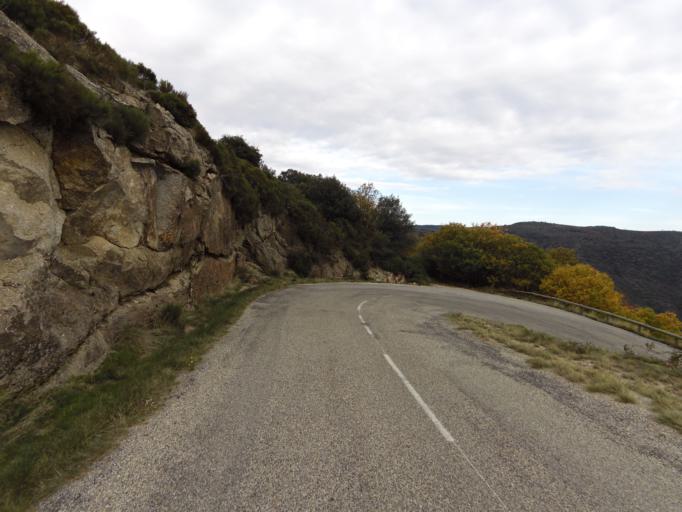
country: FR
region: Rhone-Alpes
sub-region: Departement de l'Ardeche
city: Les Vans
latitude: 44.5031
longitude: 4.0459
